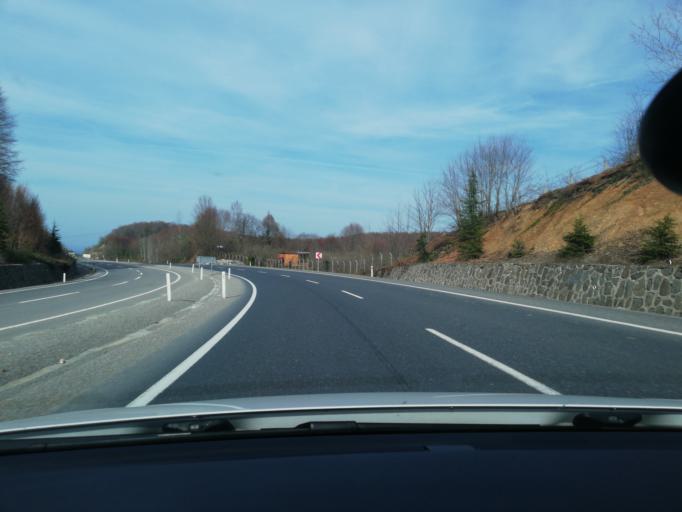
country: TR
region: Zonguldak
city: Kozlu
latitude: 41.3337
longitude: 31.6275
